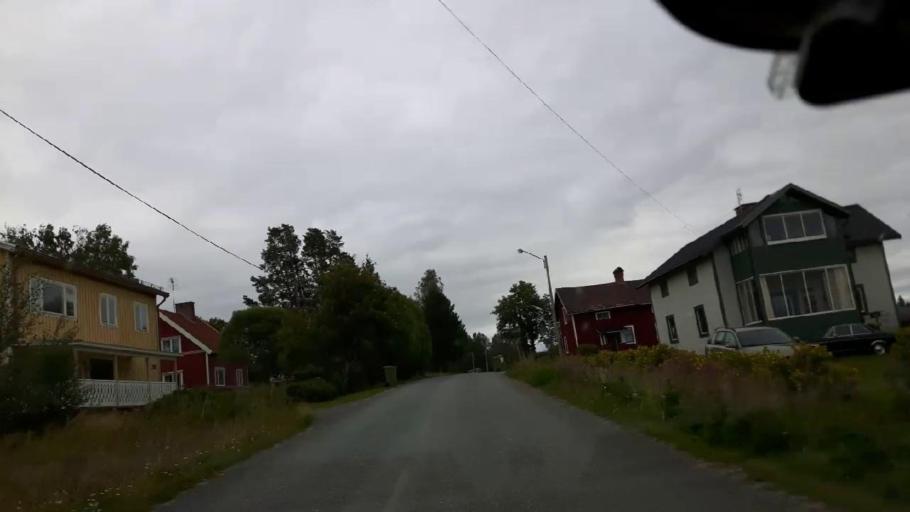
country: SE
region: Jaemtland
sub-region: Braecke Kommun
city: Braecke
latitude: 62.8419
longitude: 15.6769
